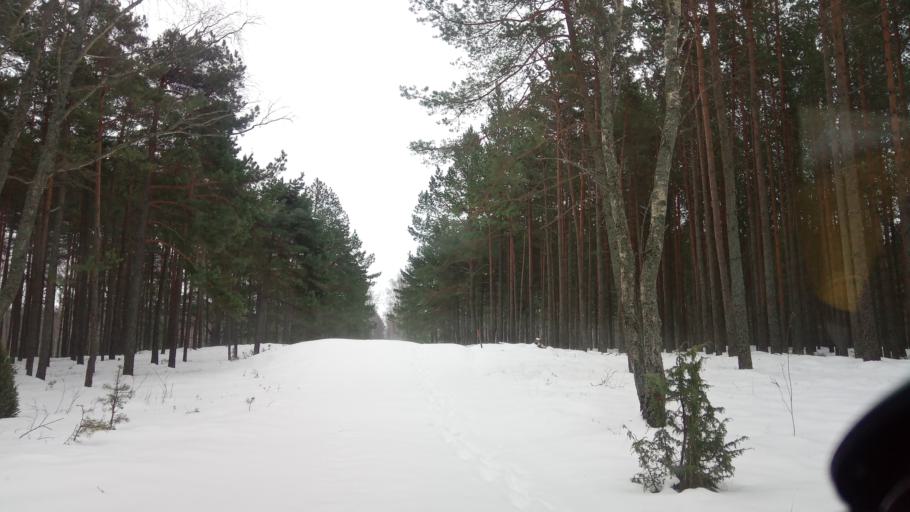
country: LT
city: Neringa
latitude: 55.4239
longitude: 21.0983
